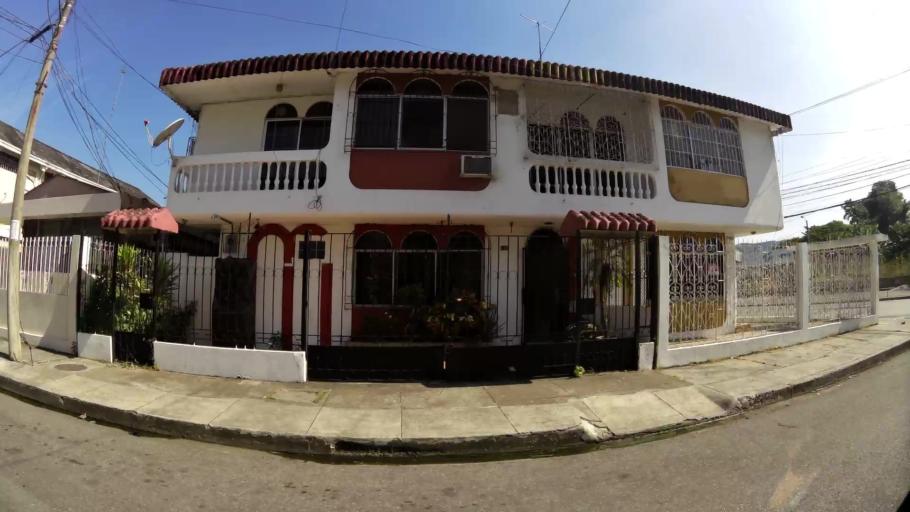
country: EC
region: Guayas
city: Guayaquil
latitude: -2.1625
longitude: -79.9208
